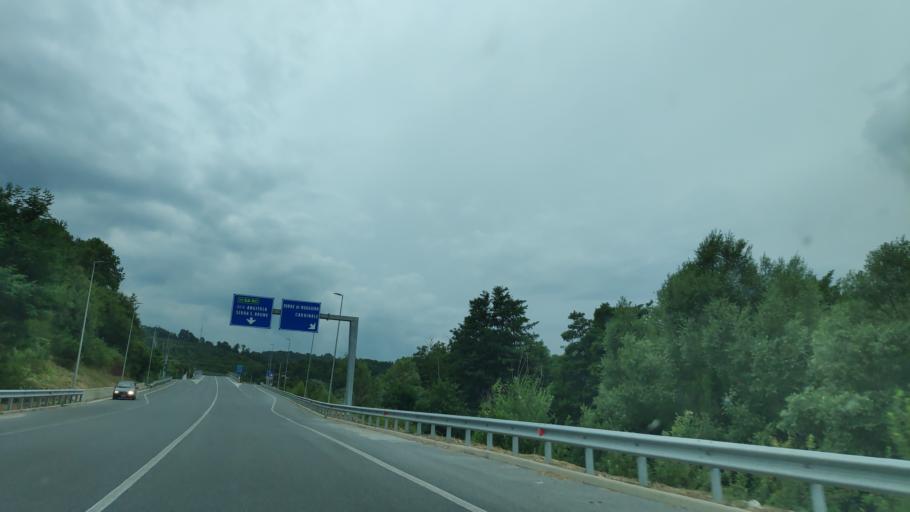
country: IT
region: Calabria
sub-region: Provincia di Catanzaro
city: Cardinale
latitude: 38.6498
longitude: 16.3805
